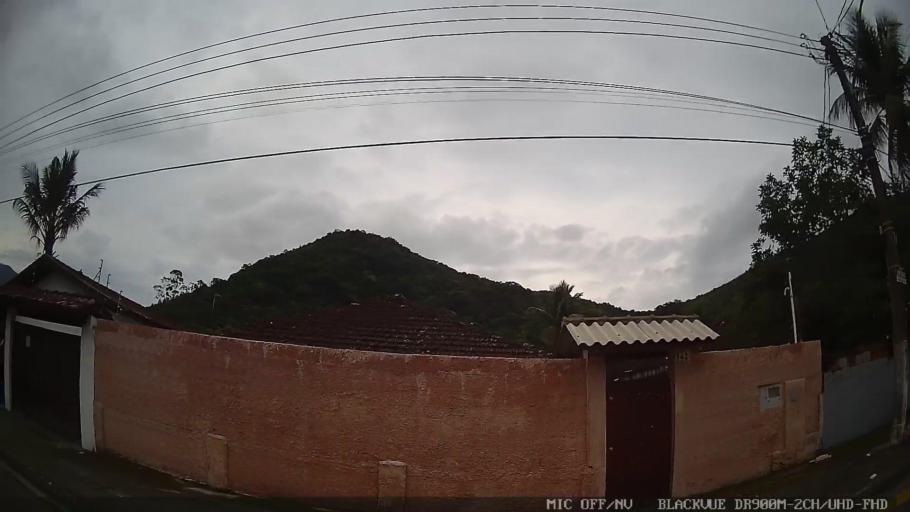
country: BR
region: Sao Paulo
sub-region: Caraguatatuba
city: Caraguatatuba
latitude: -23.6215
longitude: -45.3767
